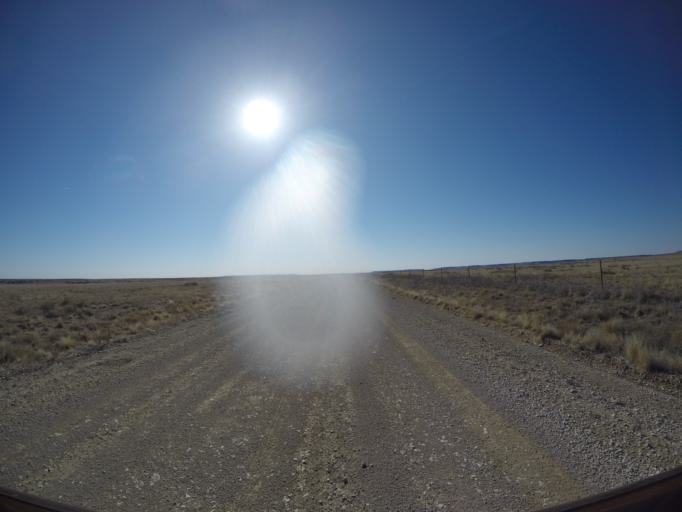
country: US
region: Colorado
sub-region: Otero County
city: La Junta
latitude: 37.6958
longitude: -103.6204
